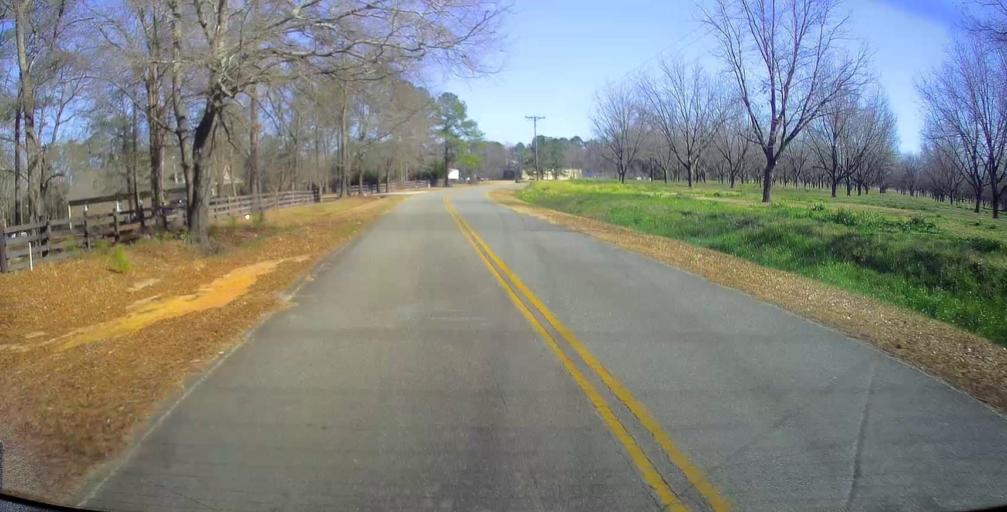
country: US
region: Georgia
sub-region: Peach County
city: Fort Valley
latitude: 32.6325
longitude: -83.8531
